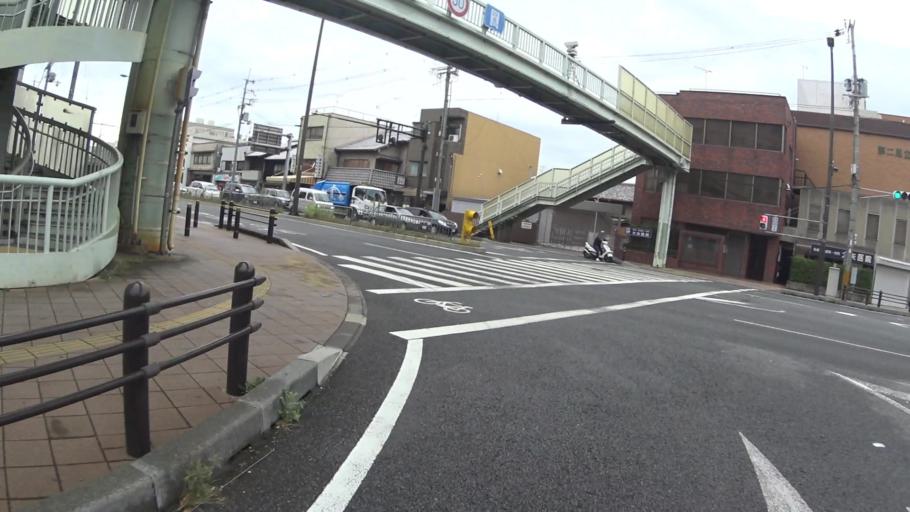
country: JP
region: Kyoto
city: Kyoto
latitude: 34.9788
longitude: 135.7455
